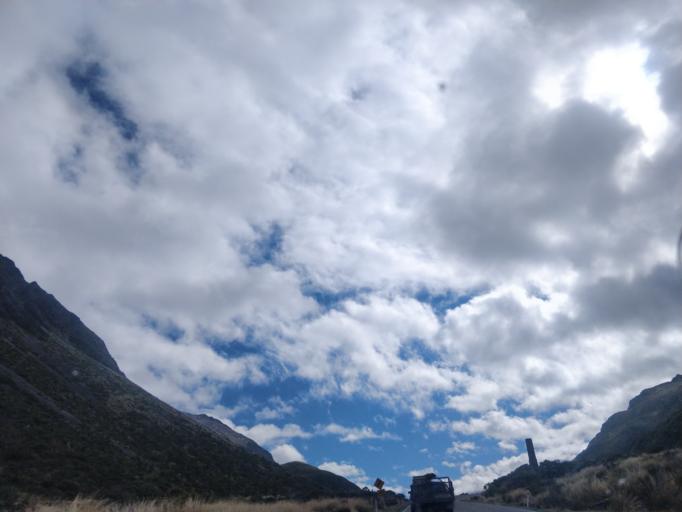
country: NZ
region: West Coast
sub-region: Grey District
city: Greymouth
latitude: -42.9092
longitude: 171.5590
